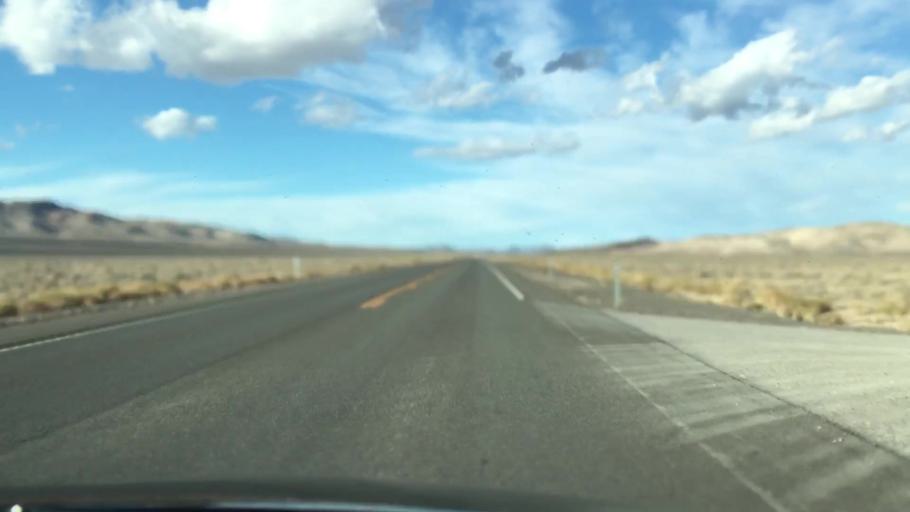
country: US
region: Nevada
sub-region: Esmeralda County
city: Goldfield
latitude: 37.5064
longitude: -117.1863
